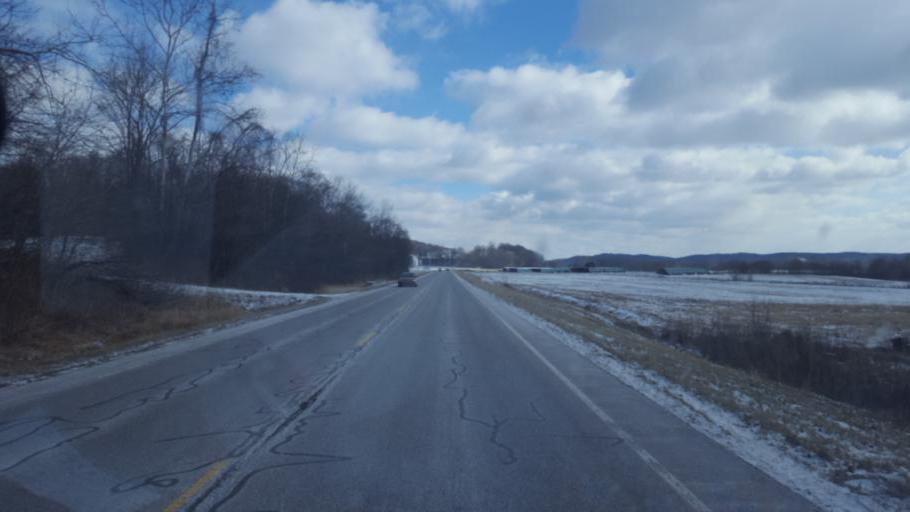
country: US
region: Ohio
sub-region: Muskingum County
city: Dresden
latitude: 40.1538
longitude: -81.9816
